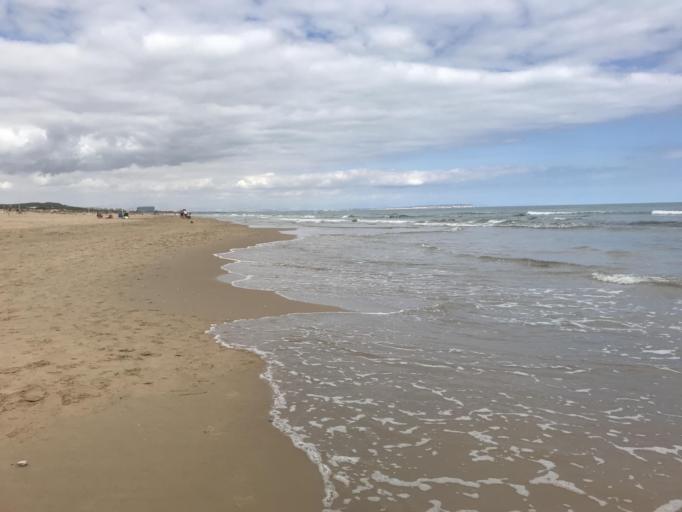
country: ES
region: Valencia
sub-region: Provincia de Alicante
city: Guardamar del Segura
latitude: 38.0346
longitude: -0.6517
